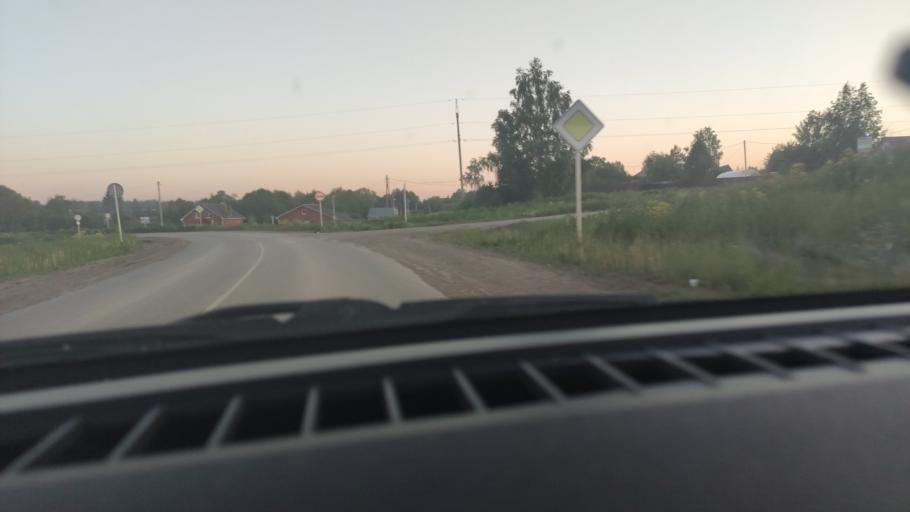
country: RU
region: Perm
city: Kultayevo
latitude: 57.8956
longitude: 55.9154
